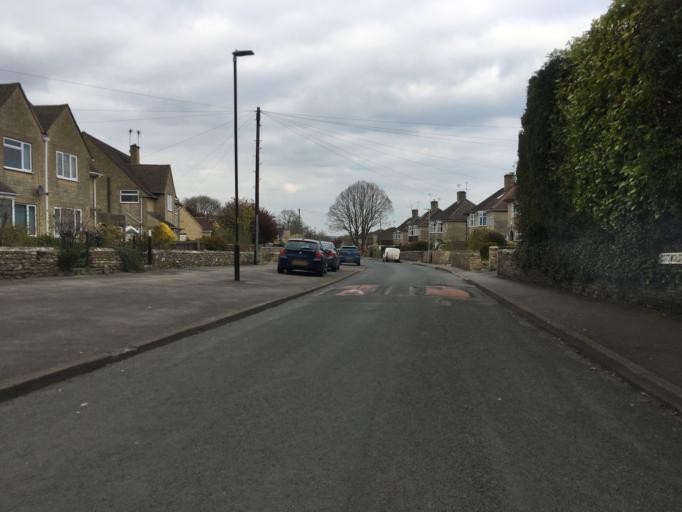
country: GB
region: England
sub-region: Gloucestershire
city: Cirencester
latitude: 51.7093
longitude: -1.9739
